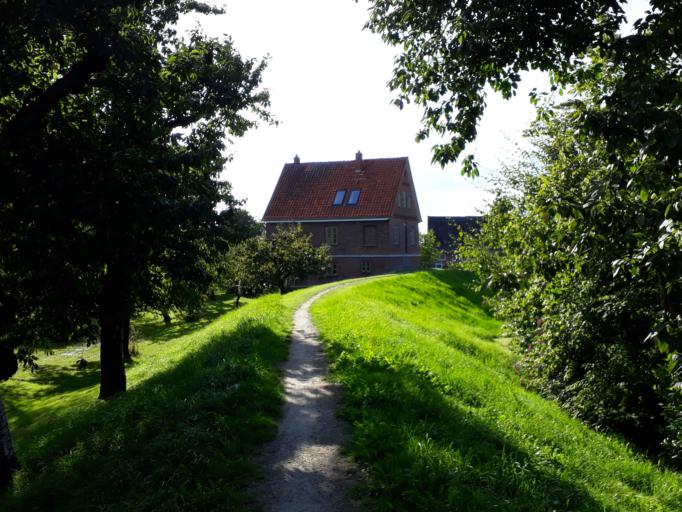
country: DE
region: Lower Saxony
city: Jork
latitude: 53.5271
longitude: 9.7349
